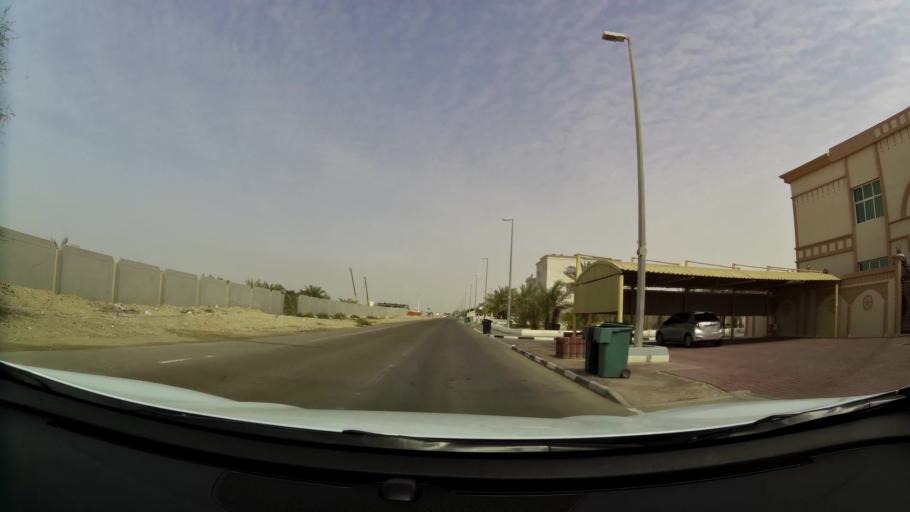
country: AE
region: Abu Dhabi
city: Abu Dhabi
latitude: 24.5318
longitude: 54.6673
